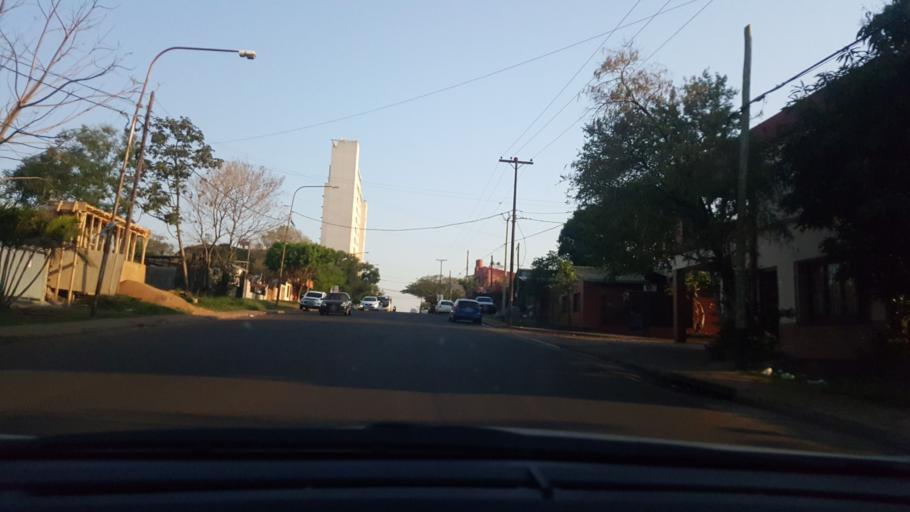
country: AR
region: Misiones
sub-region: Departamento de Capital
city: Posadas
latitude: -27.3802
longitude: -55.8880
